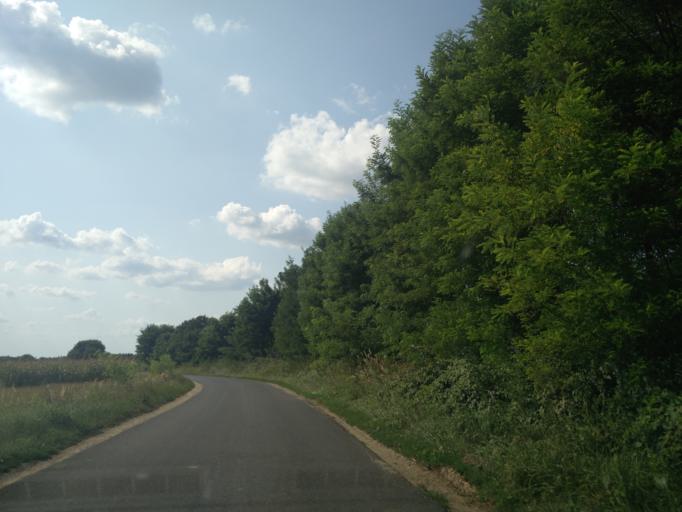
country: HU
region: Zala
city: Zalaegerszeg
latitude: 46.8960
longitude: 16.7906
